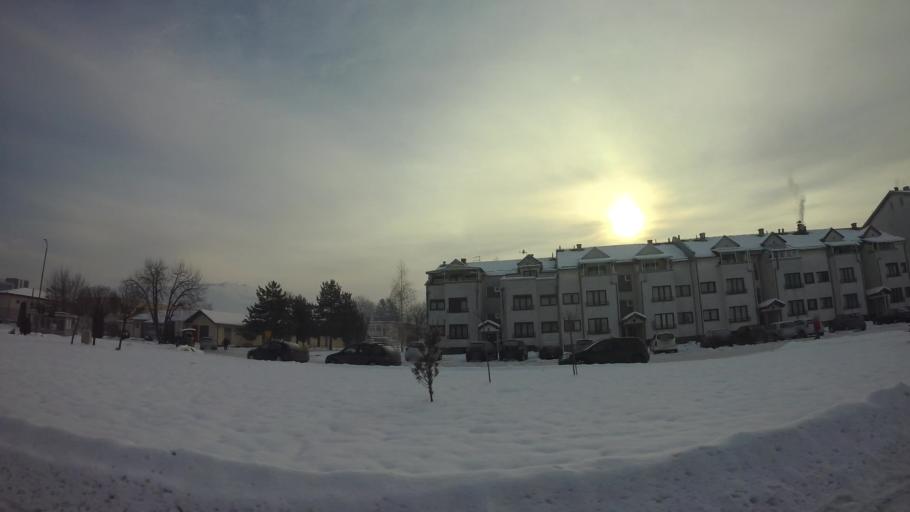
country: BA
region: Federation of Bosnia and Herzegovina
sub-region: Kanton Sarajevo
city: Sarajevo
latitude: 43.8157
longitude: 18.3537
